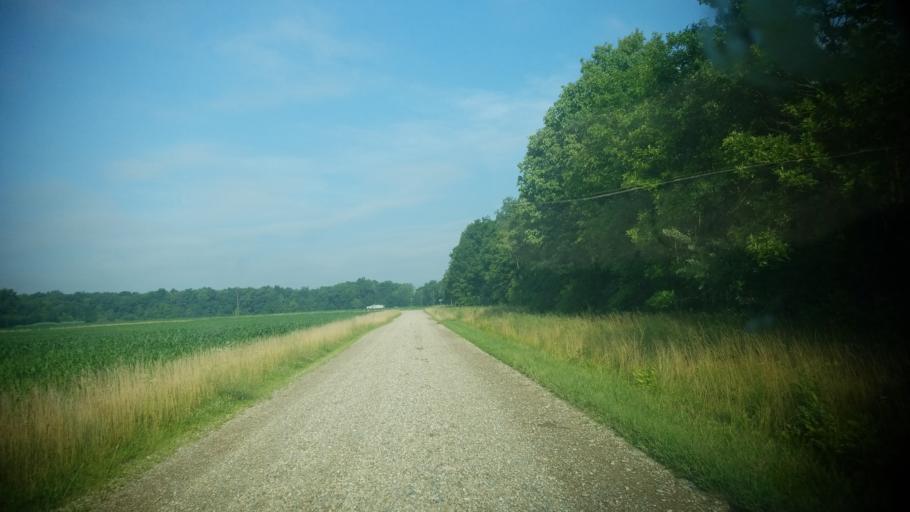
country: US
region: Illinois
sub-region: Clay County
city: Flora
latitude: 38.6021
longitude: -88.3618
